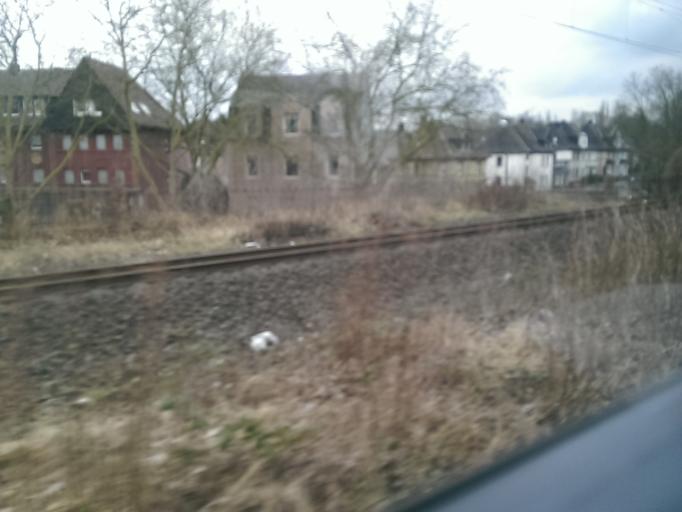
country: DE
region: North Rhine-Westphalia
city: Lunen
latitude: 51.6190
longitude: 7.5300
